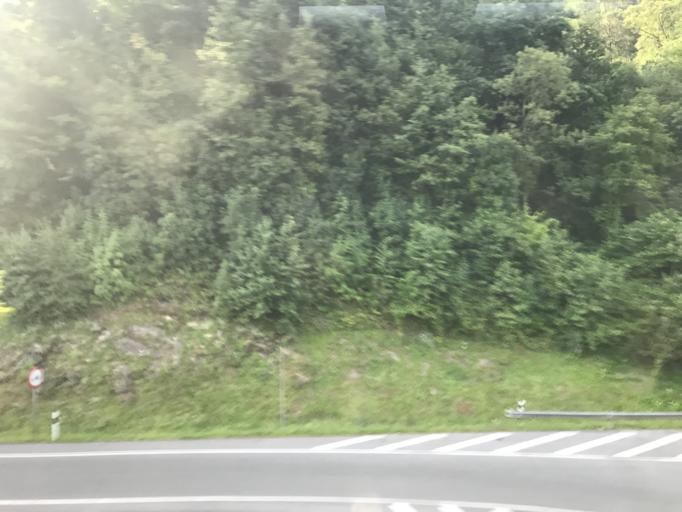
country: ES
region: Basque Country
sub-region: Provincia de Guipuzcoa
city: Icazteguieta
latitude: 43.0951
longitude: -2.1137
